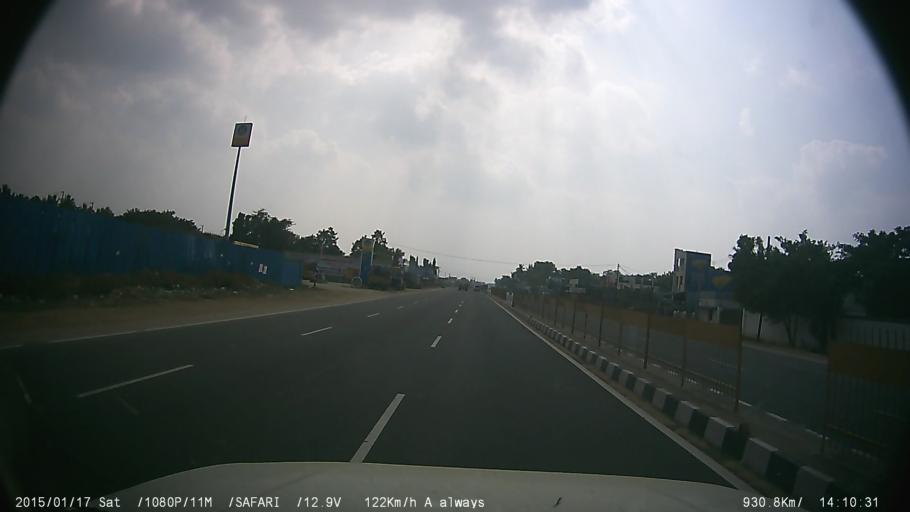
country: IN
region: Tamil Nadu
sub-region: Vellore
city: Ambur
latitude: 12.8042
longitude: 78.7368
